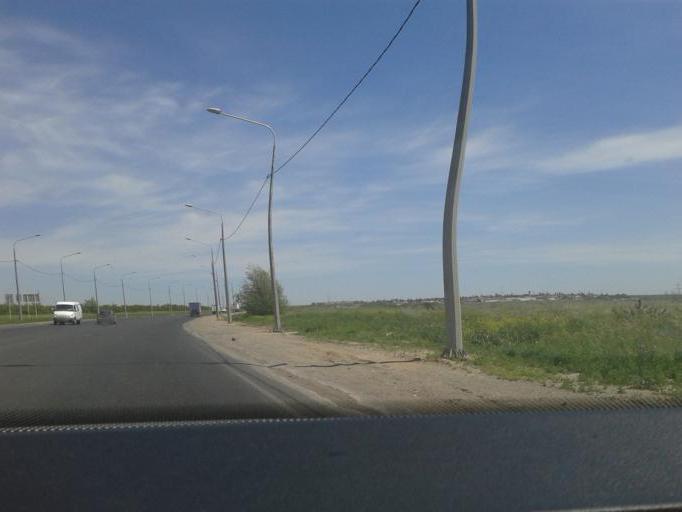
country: RU
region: Volgograd
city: Vodstroy
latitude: 48.8247
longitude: 44.5267
